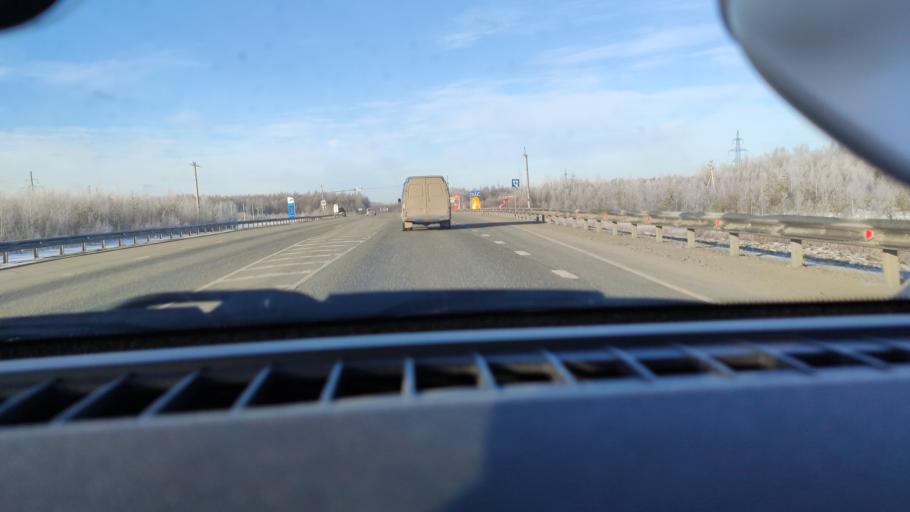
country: RU
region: Perm
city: Krasnokamsk
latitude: 58.1010
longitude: 55.7489
